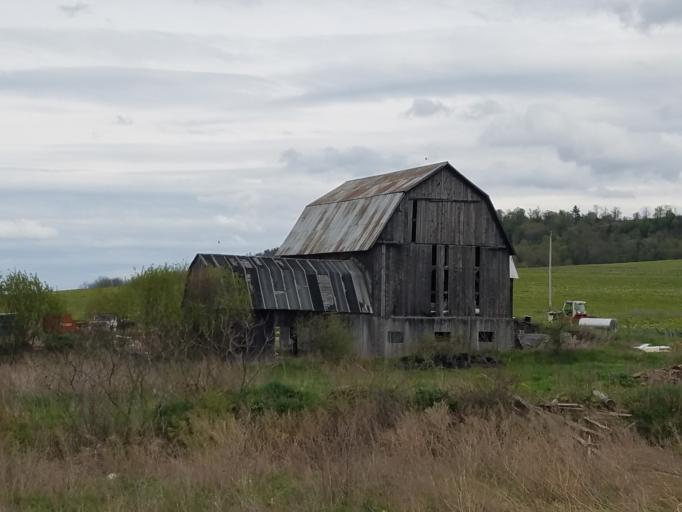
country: US
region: New York
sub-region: Steuben County
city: Canisteo
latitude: 42.1132
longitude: -77.4917
